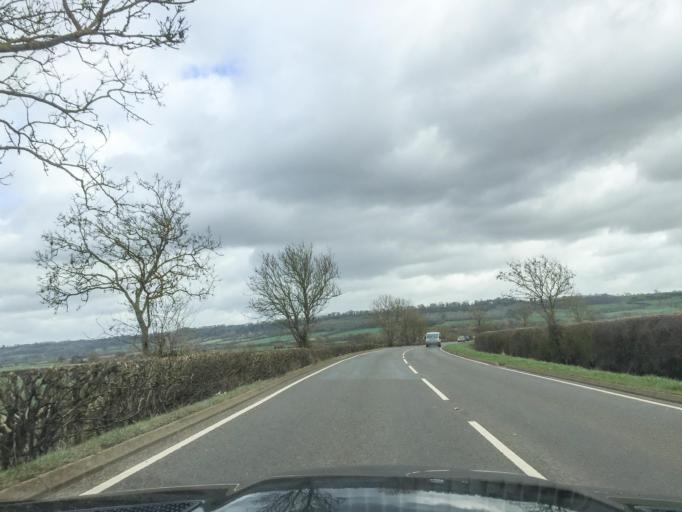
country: GB
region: England
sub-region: Warwickshire
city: Wellesbourne Mountford
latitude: 52.1208
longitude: -1.5068
